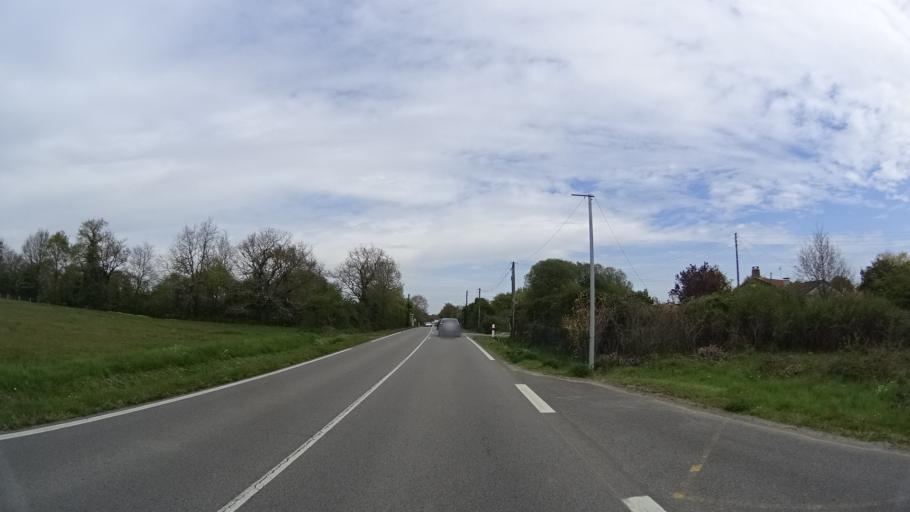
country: FR
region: Pays de la Loire
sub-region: Departement de la Loire-Atlantique
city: Bourgneuf-en-Retz
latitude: 47.0580
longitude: -1.9204
